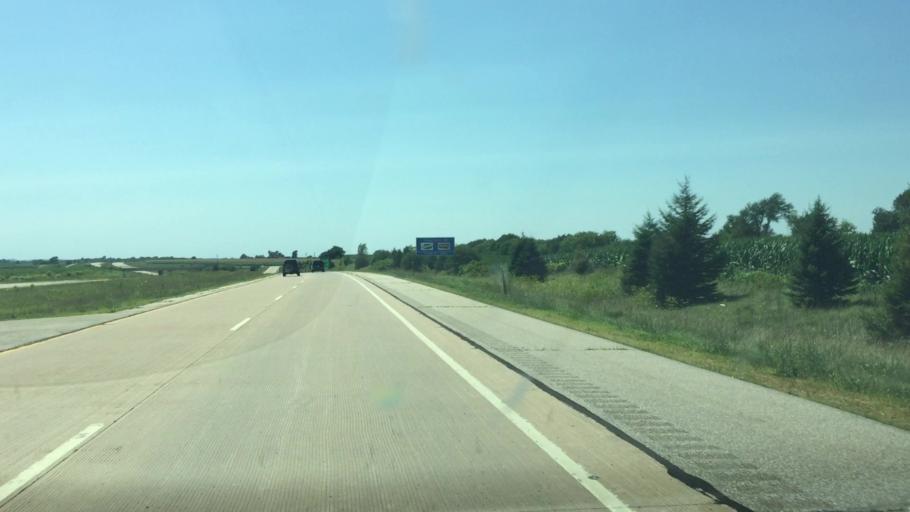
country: US
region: Wisconsin
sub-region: Grant County
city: Platteville
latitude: 42.7138
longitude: -90.4754
